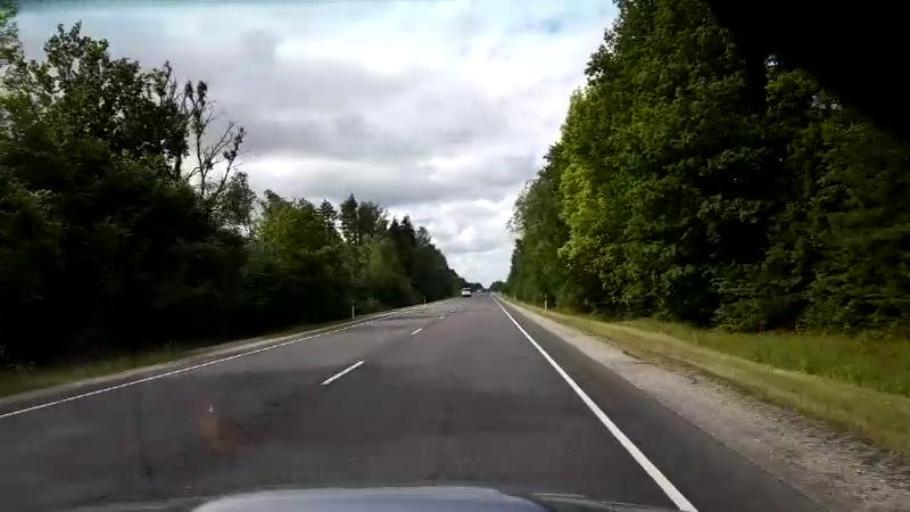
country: EE
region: Raplamaa
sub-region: Maerjamaa vald
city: Marjamaa
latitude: 58.8674
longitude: 24.4404
